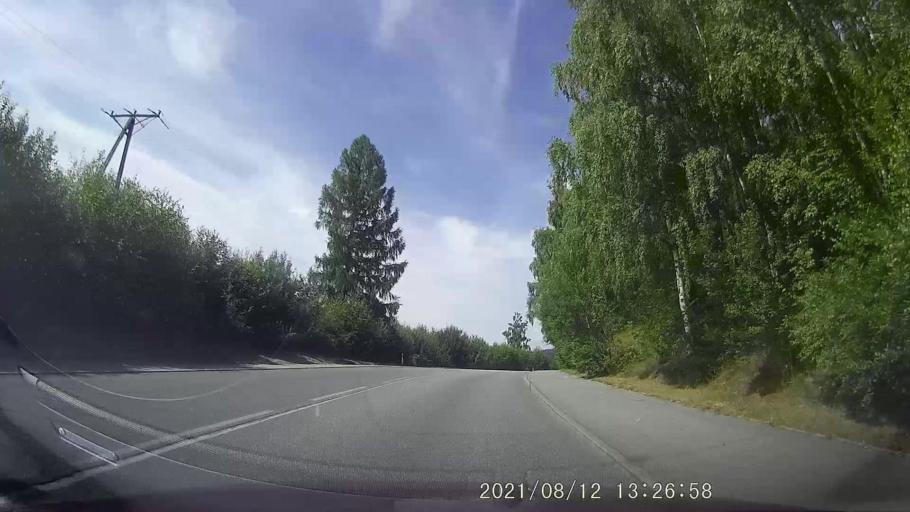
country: PL
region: Lower Silesian Voivodeship
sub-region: Powiat klodzki
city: Ladek-Zdroj
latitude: 50.3293
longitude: 16.8712
